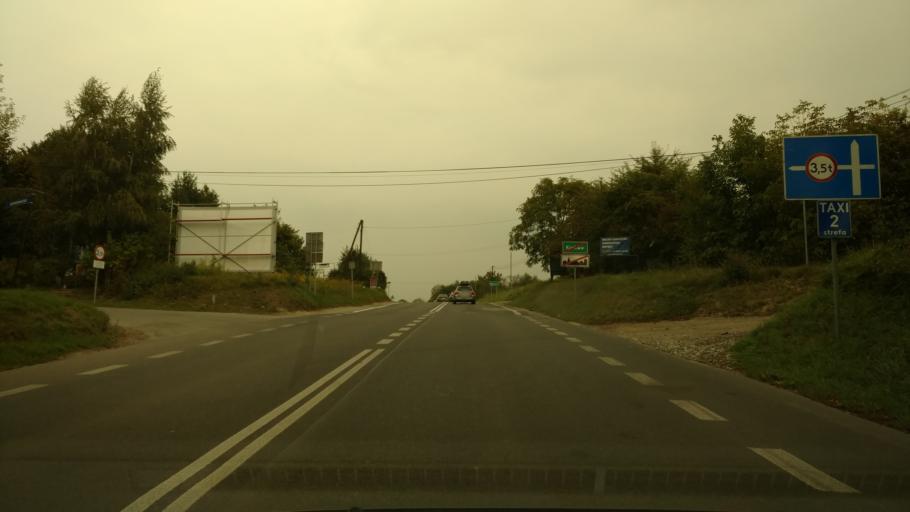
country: PL
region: Lesser Poland Voivodeship
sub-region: Powiat krakowski
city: Zielonki
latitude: 50.1085
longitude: 19.9655
